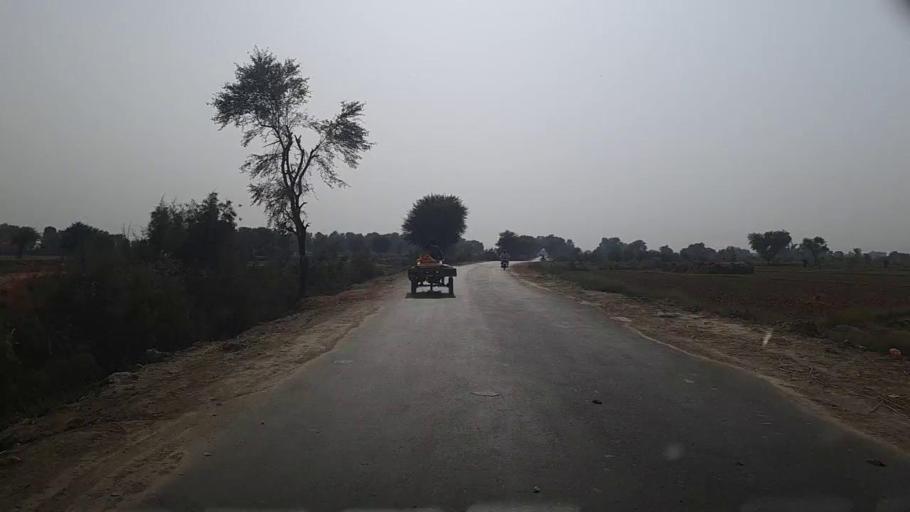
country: PK
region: Sindh
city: Kashmor
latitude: 28.4120
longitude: 69.5657
